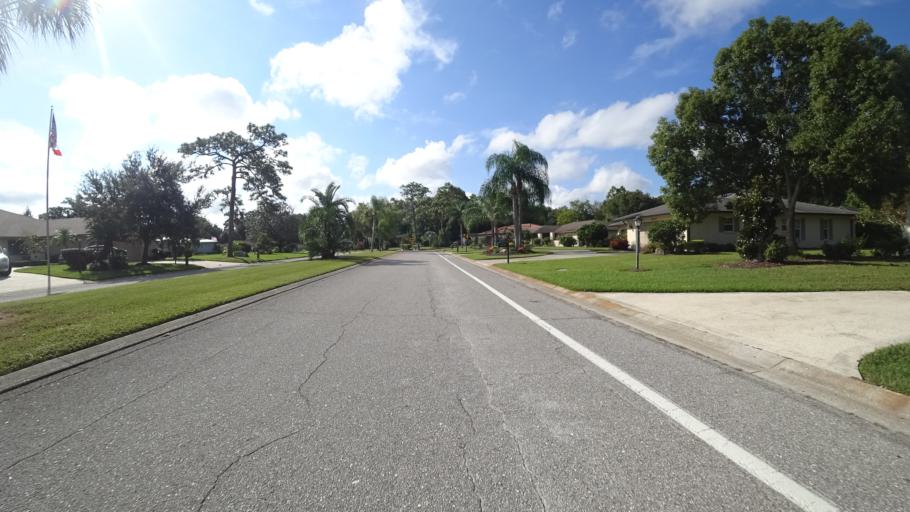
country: US
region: Florida
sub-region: Sarasota County
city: Desoto Lakes
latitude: 27.4013
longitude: -82.5010
